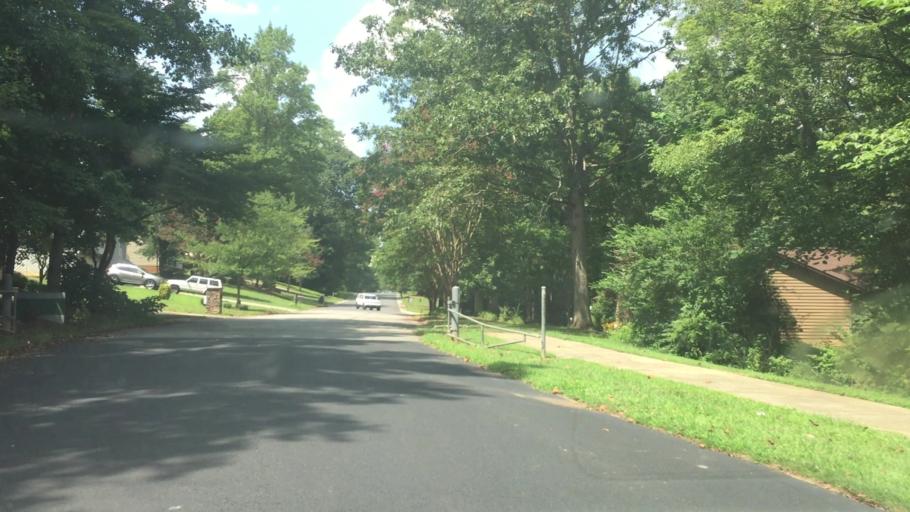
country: US
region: North Carolina
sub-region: Iredell County
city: Mooresville
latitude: 35.5521
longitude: -80.8000
